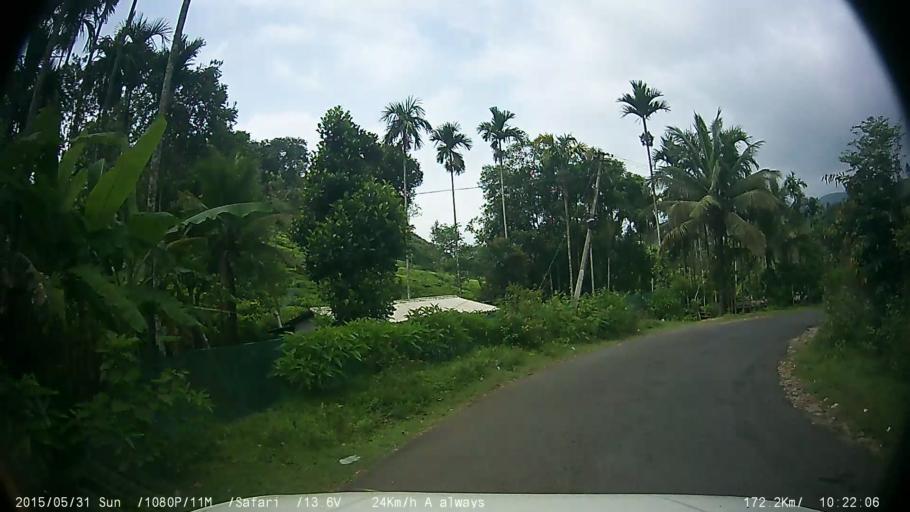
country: IN
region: Kerala
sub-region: Wayanad
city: Kalpetta
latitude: 11.5396
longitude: 76.1357
